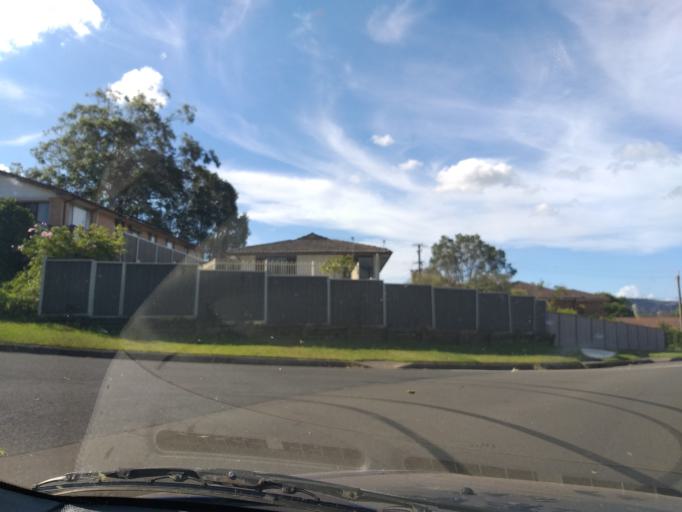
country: AU
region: New South Wales
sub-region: Wollongong
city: Koonawarra
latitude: -34.4945
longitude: 150.8156
